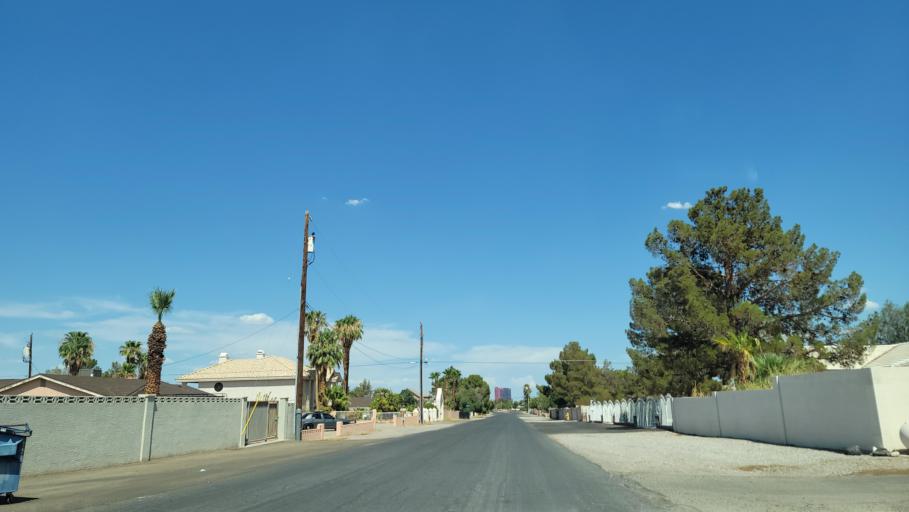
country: US
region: Nevada
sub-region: Clark County
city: Spring Valley
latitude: 36.1348
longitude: -115.2294
